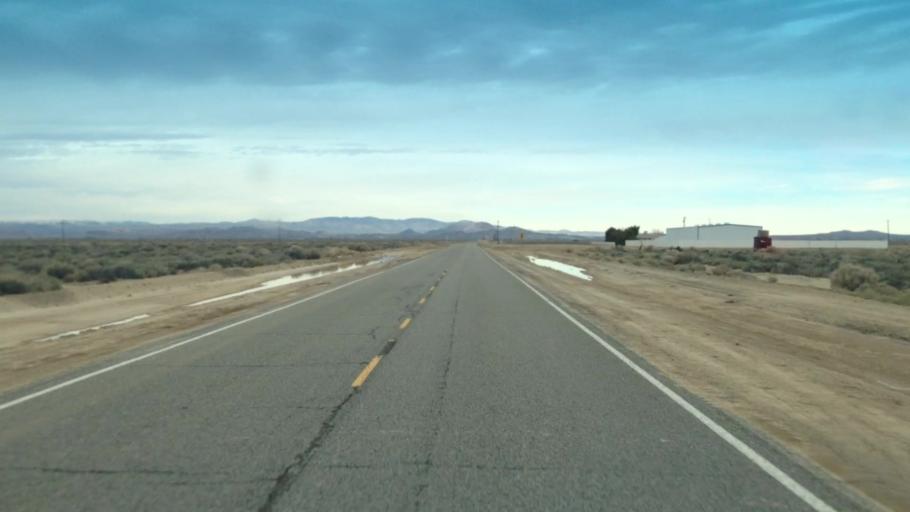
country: US
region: California
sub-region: Los Angeles County
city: Lancaster
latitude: 34.7440
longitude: -118.1842
